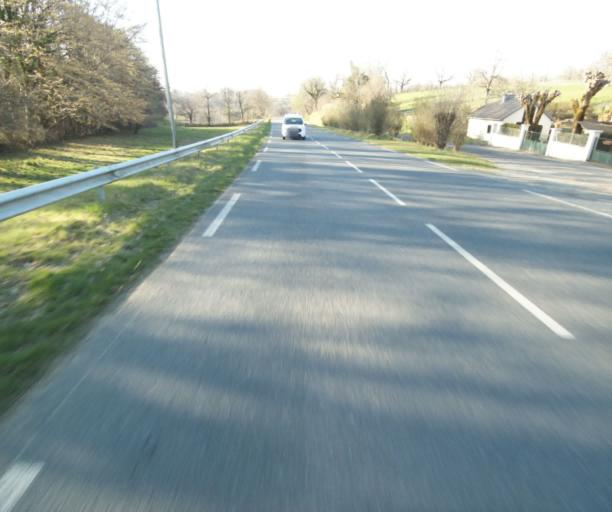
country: FR
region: Limousin
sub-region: Departement de la Correze
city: Seilhac
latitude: 45.3897
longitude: 1.7213
